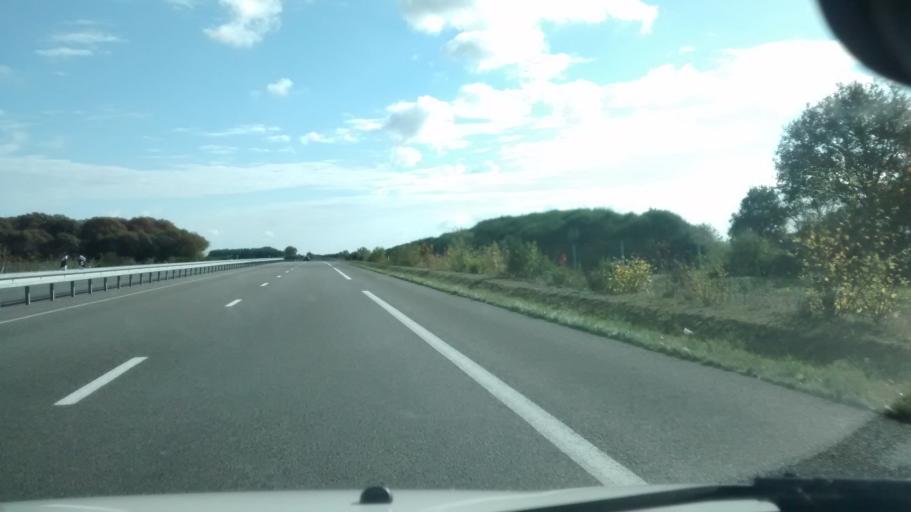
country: FR
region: Pays de la Loire
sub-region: Departement de Maine-et-Loire
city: Combree
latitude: 47.7252
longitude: -1.0556
